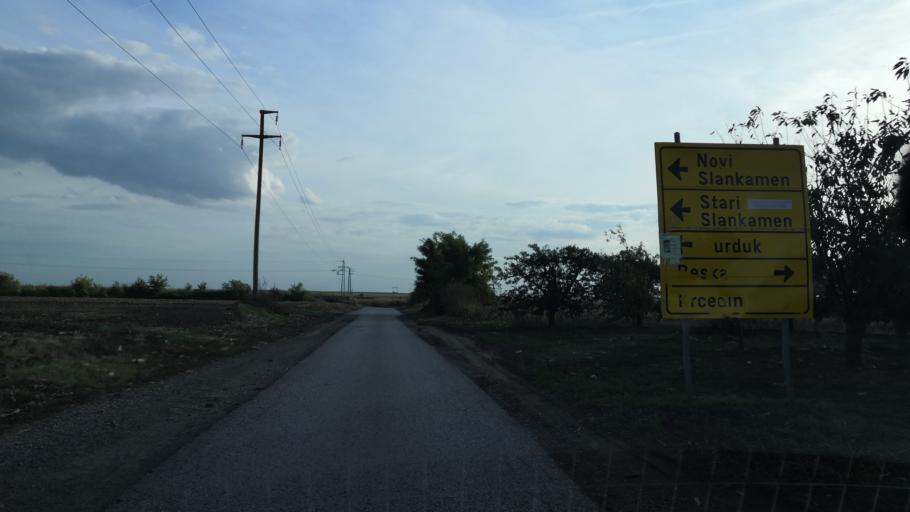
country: RS
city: Krcedin
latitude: 45.1422
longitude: 20.1872
